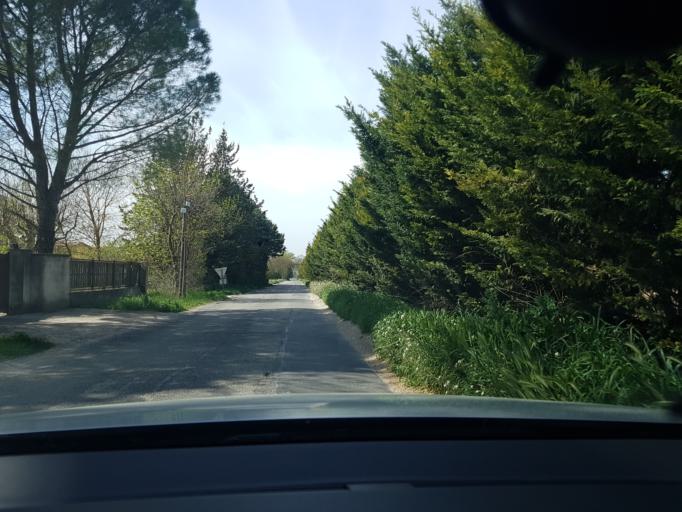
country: FR
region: Provence-Alpes-Cote d'Azur
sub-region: Departement des Bouches-du-Rhone
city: Bouc-Bel-Air
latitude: 43.4755
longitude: 5.3915
